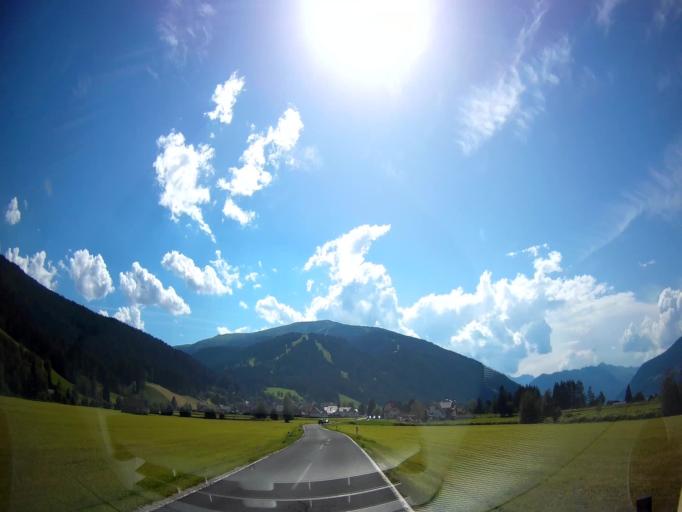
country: AT
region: Salzburg
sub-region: Politischer Bezirk Tamsweg
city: Sankt Margarethen im Lungau
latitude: 47.0844
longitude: 13.7069
